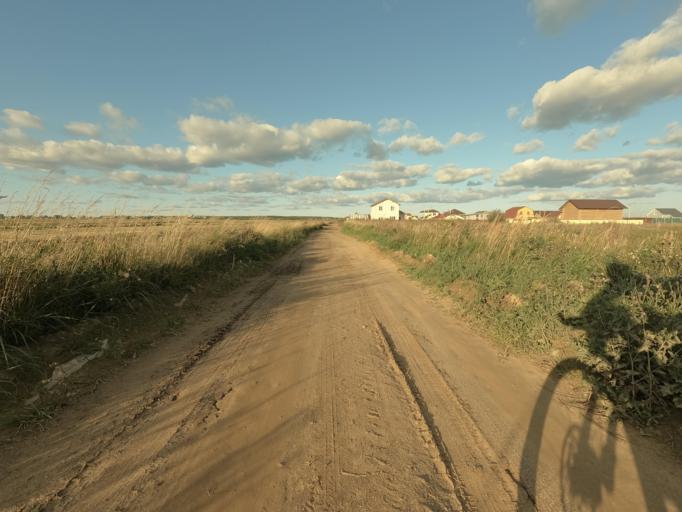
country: RU
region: Leningrad
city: Imeni Sverdlova
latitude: 59.8671
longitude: 30.7314
